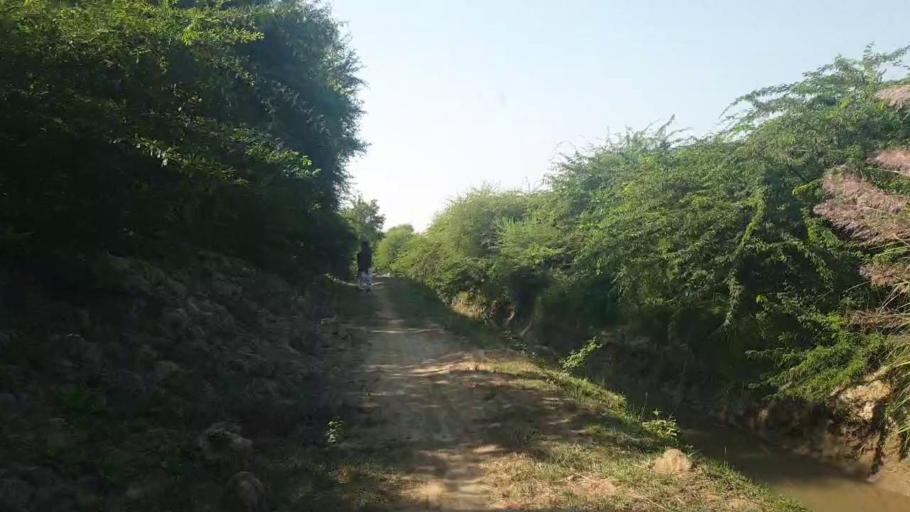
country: PK
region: Sindh
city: Badin
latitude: 24.7239
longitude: 68.8776
